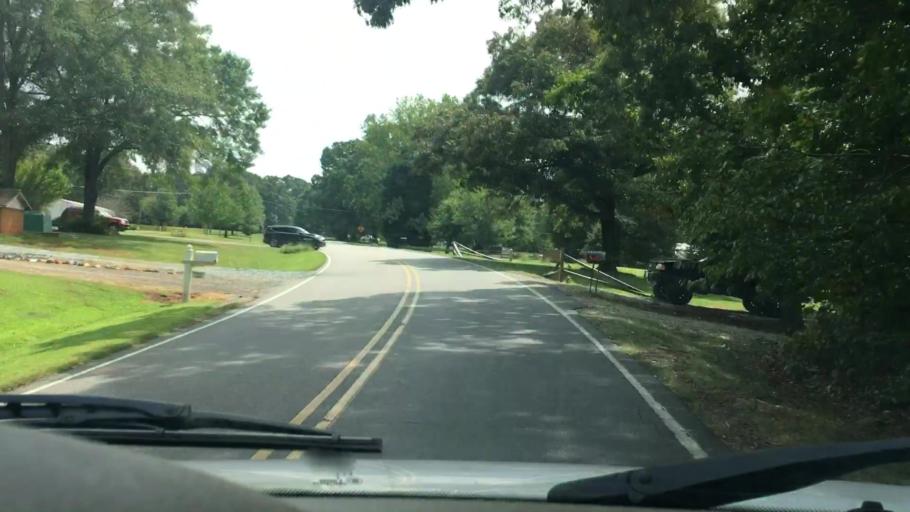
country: US
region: North Carolina
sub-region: Gaston County
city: Davidson
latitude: 35.5095
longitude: -80.7987
